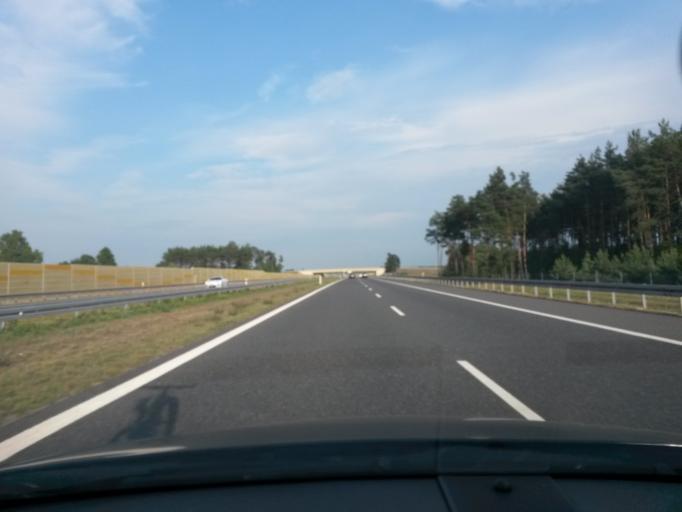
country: PL
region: Lodz Voivodeship
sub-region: Powiat zgierski
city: Ozorkow
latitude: 51.9338
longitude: 19.2728
